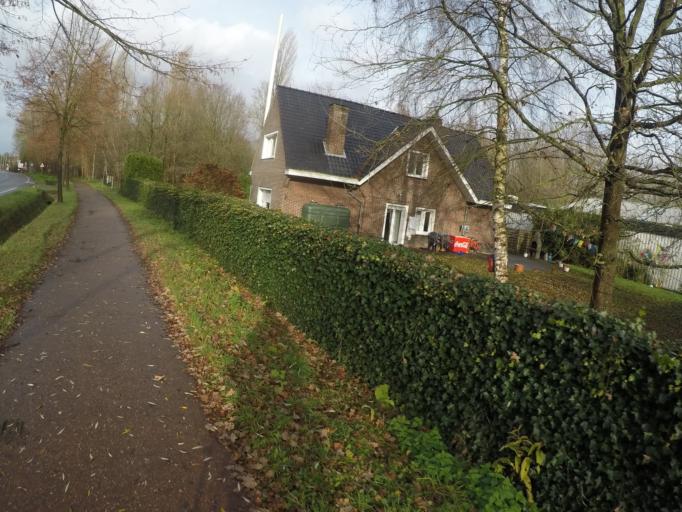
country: BE
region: Flanders
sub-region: Provincie Antwerpen
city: Wijnegem
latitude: 51.2208
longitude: 4.5256
